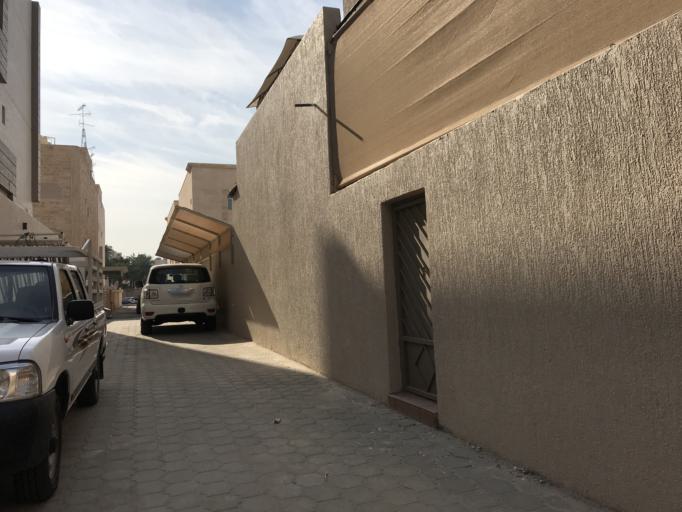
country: KW
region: Muhafazat Hawalli
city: Ar Rumaythiyah
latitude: 29.3039
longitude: 48.0744
